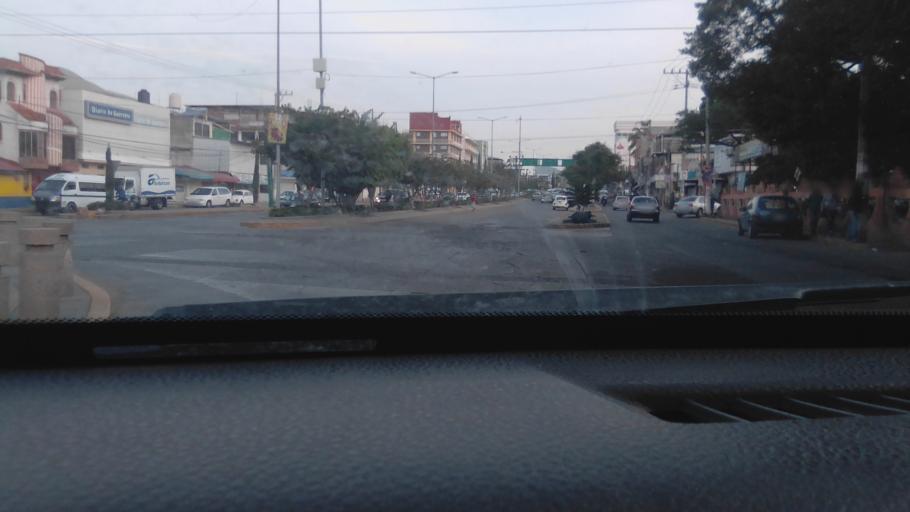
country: MX
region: Guerrero
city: Chilpancingo de los Bravos
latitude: 17.5600
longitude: -99.5063
